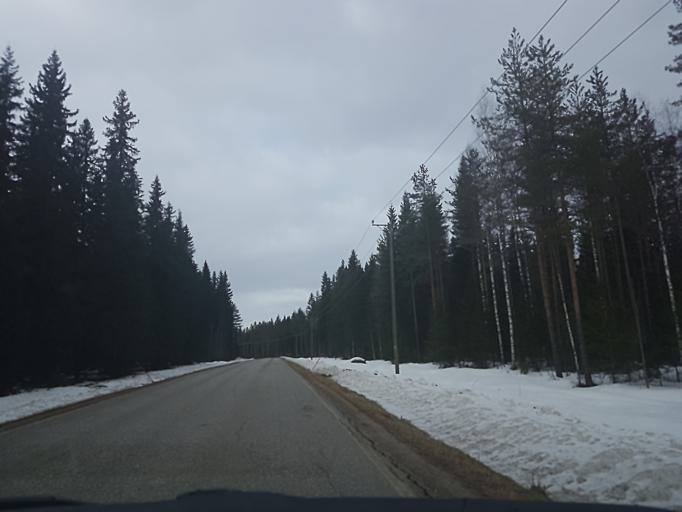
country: FI
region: Northern Savo
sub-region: Koillis-Savo
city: Kaavi
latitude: 63.0188
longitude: 28.6509
